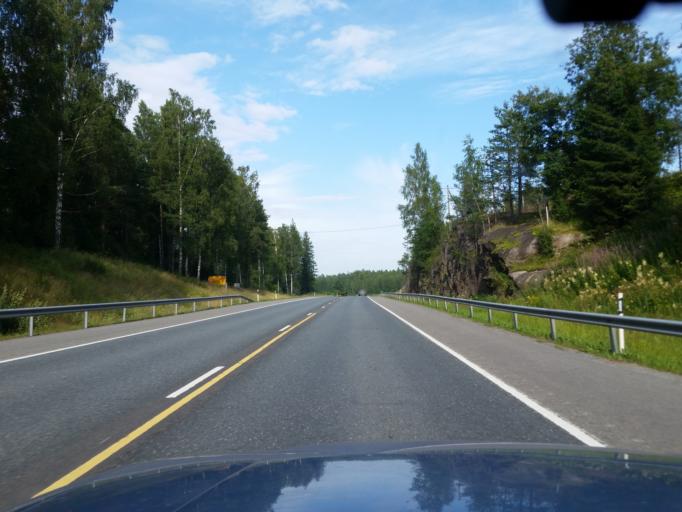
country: FI
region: Uusimaa
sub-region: Helsinki
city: Siuntio
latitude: 60.0881
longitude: 24.2031
